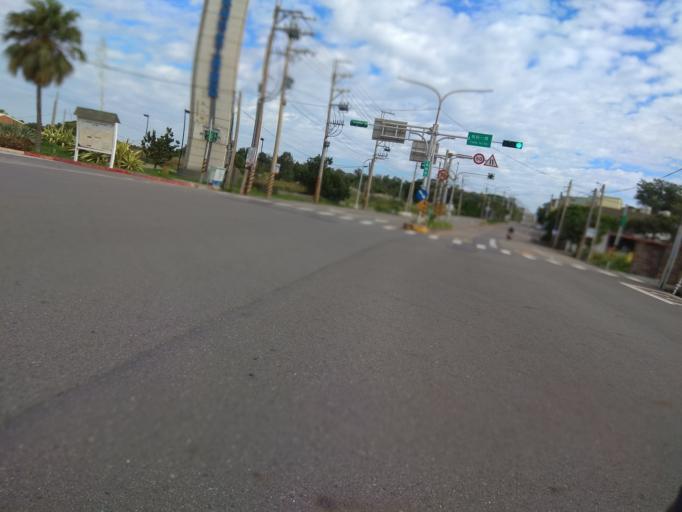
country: TW
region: Taiwan
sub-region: Hsinchu
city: Zhubei
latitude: 25.0334
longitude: 121.0723
